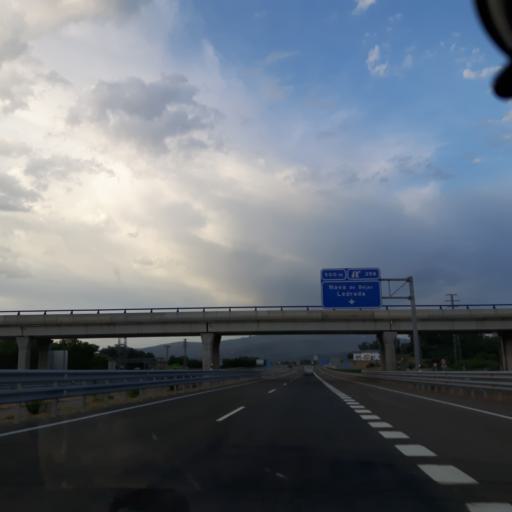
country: ES
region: Castille and Leon
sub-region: Provincia de Salamanca
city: Nava de Bejar
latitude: 40.4890
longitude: -5.6767
